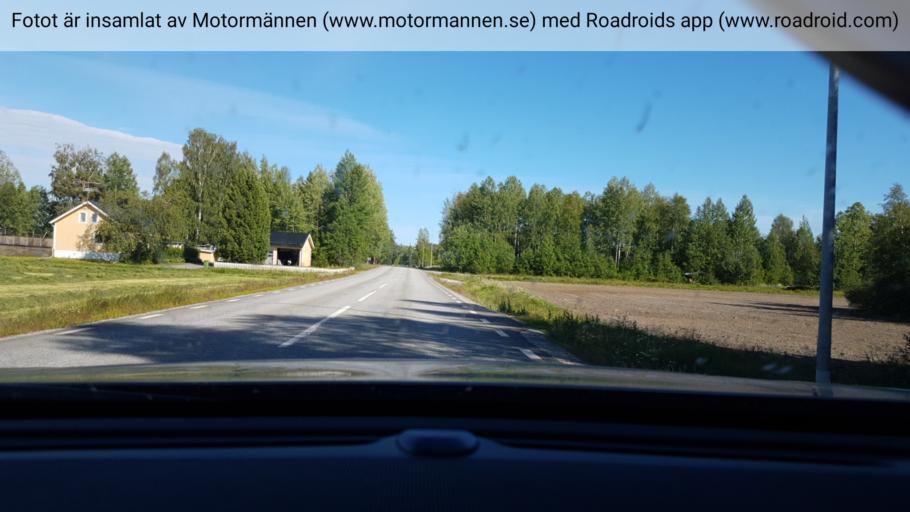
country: SE
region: Vaesterbotten
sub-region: Lycksele Kommun
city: Lycksele
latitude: 64.6341
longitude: 18.5445
